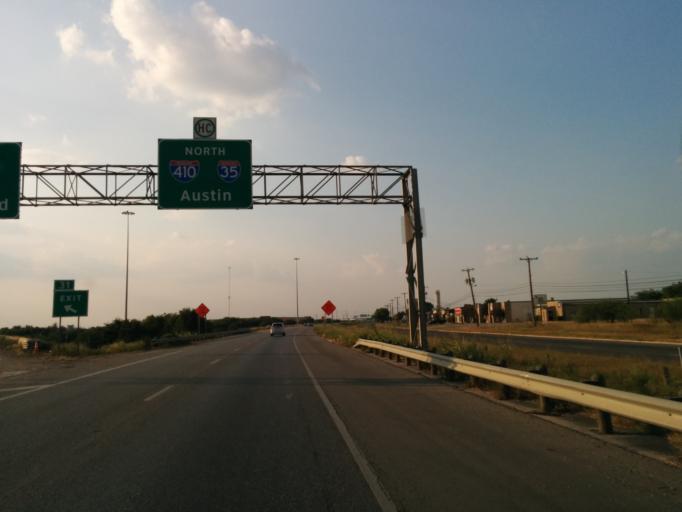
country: US
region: Texas
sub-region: Bexar County
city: Kirby
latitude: 29.4502
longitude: -98.4033
